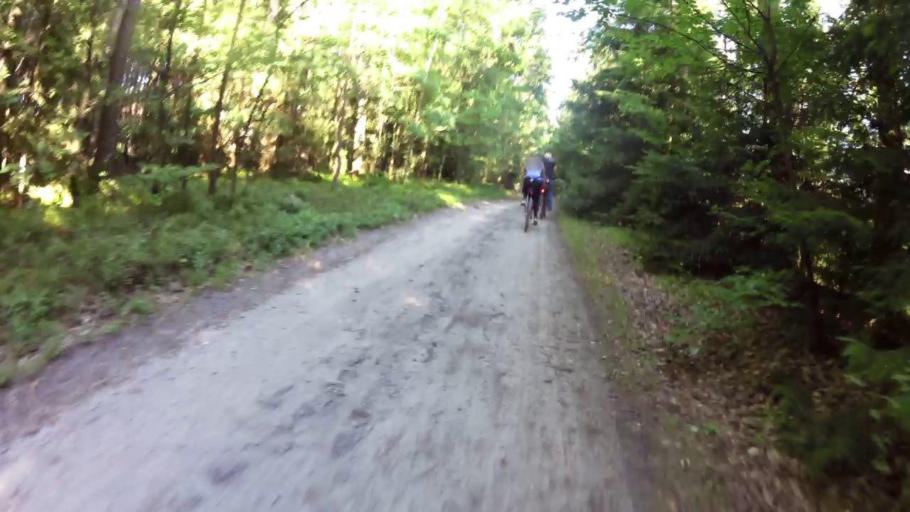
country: PL
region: West Pomeranian Voivodeship
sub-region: Powiat bialogardzki
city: Tychowo
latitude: 53.9483
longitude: 16.1203
